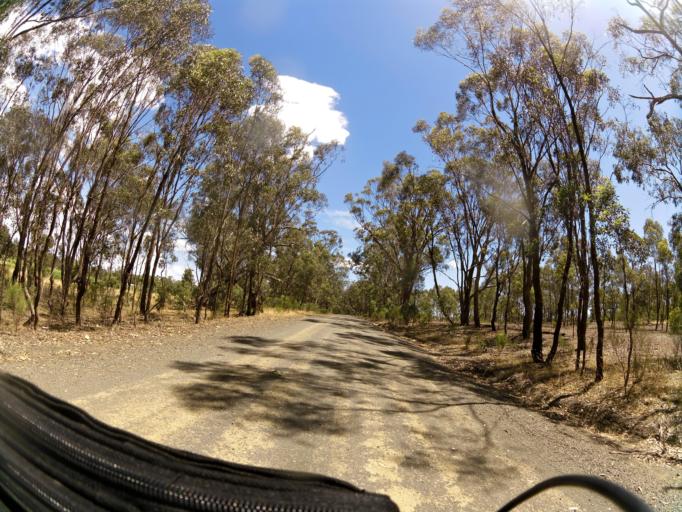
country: AU
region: Victoria
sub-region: Campaspe
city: Kyabram
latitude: -36.7966
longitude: 145.0810
